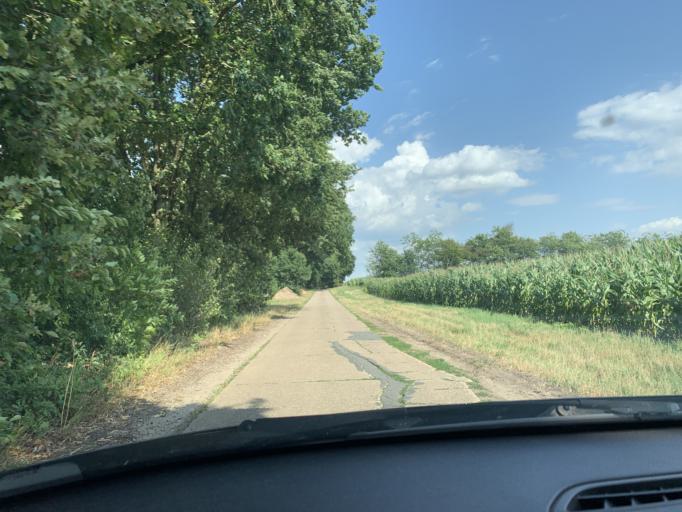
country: DE
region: Lower Saxony
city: Handeloh
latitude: 53.2218
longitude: 9.9071
